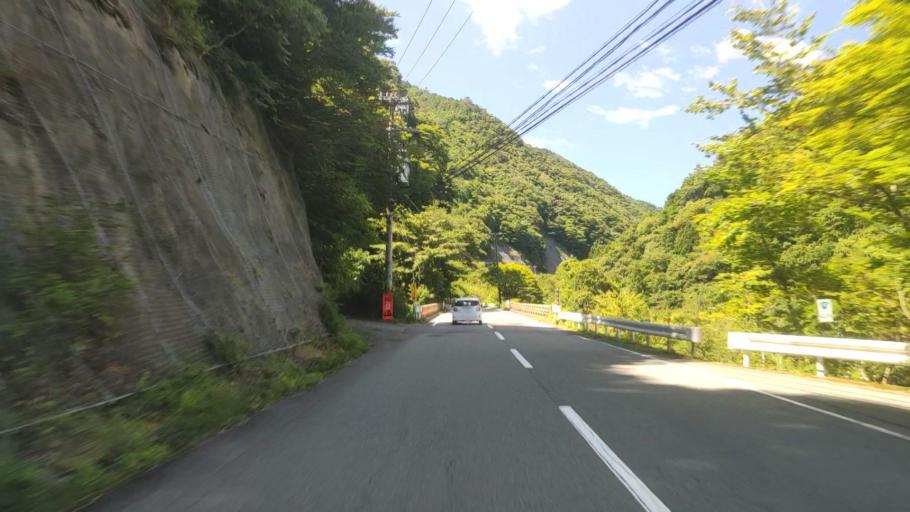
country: JP
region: Nara
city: Yoshino-cho
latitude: 34.2029
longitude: 135.9984
